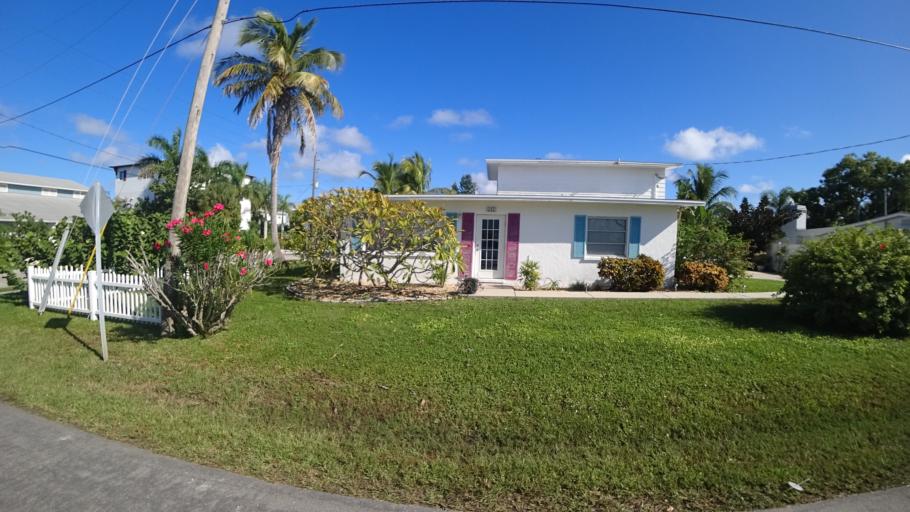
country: US
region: Florida
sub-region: Manatee County
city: Anna Maria
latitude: 27.5298
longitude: -82.7263
